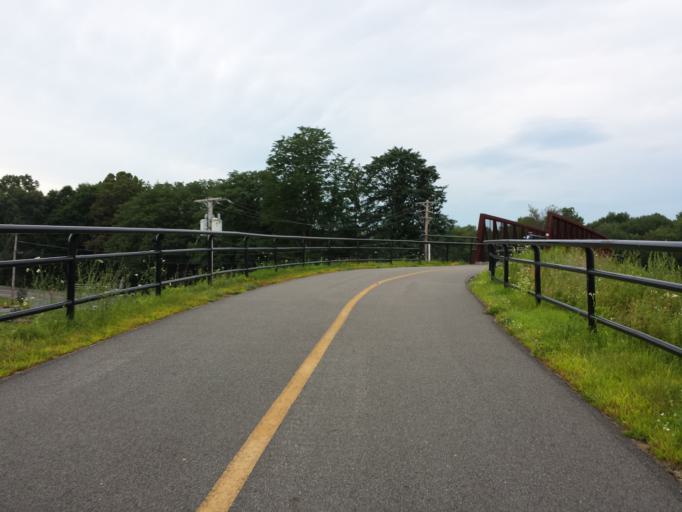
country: US
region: New York
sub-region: Dutchess County
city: Myers Corner
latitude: 41.6071
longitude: -73.8396
